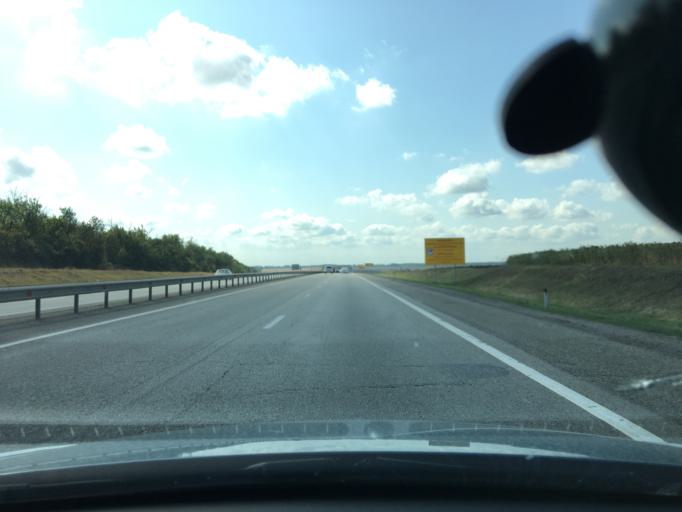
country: RU
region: Krasnodarskiy
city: Krasnoye
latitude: 46.7828
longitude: 39.6651
